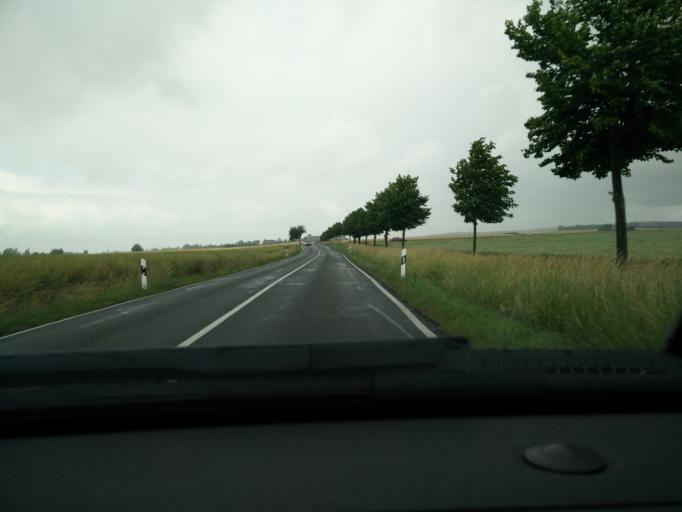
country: DE
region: Saxony
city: Grossbardau
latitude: 51.1892
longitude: 12.6945
